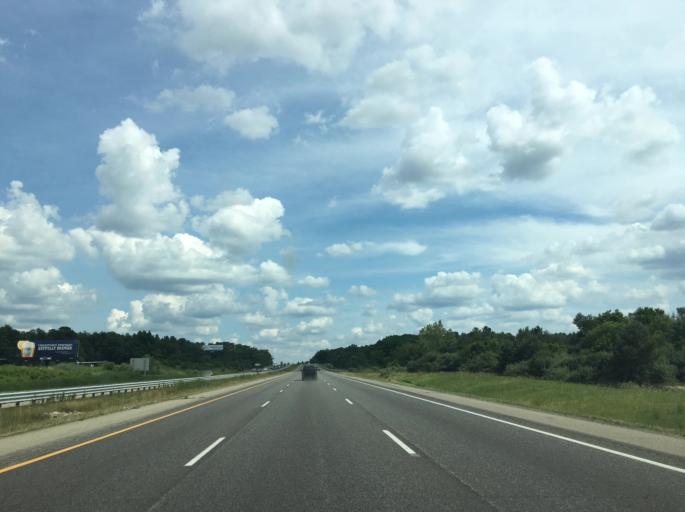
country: US
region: Michigan
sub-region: Genesee County
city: Grand Blanc
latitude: 42.8860
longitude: -83.6195
